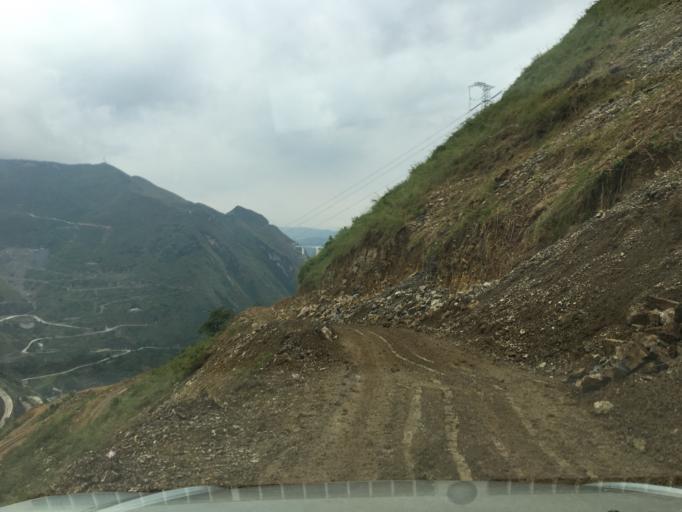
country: CN
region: Guizhou Sheng
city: Liupanshui
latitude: 25.9630
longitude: 105.2380
